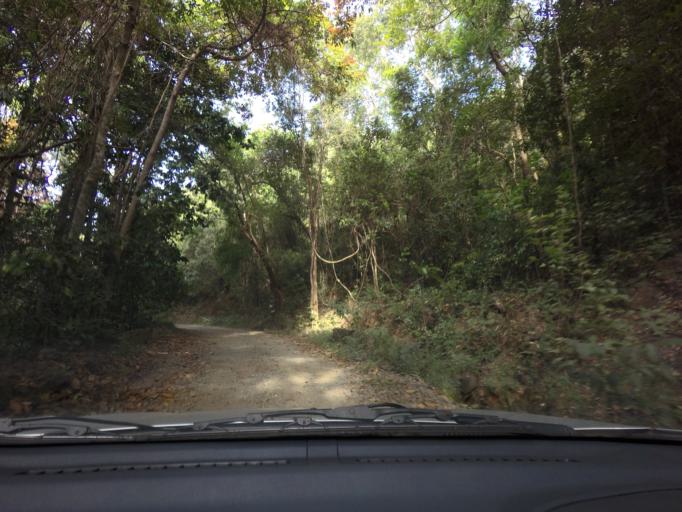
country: IN
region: Karnataka
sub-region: Kodagu
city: Somvarpet
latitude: 12.7197
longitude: 75.6651
